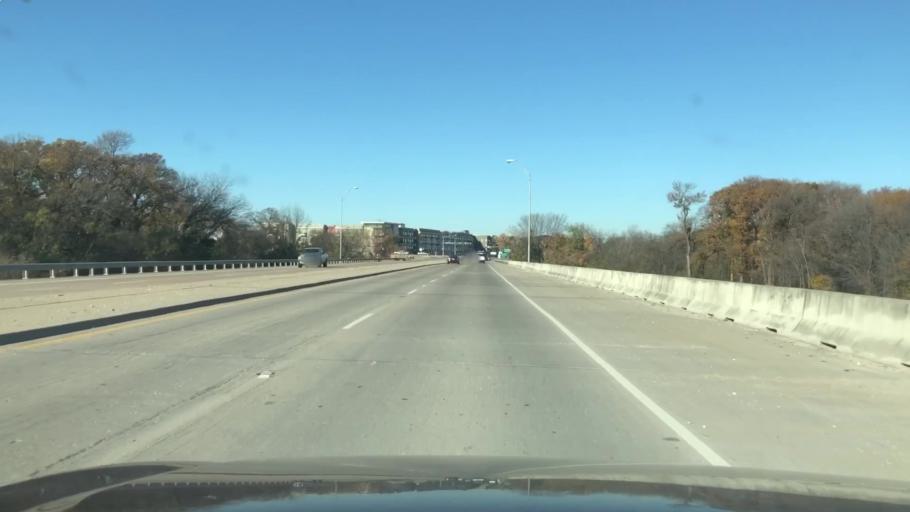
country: US
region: Texas
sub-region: Dallas County
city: Irving
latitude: 32.8734
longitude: -96.9291
